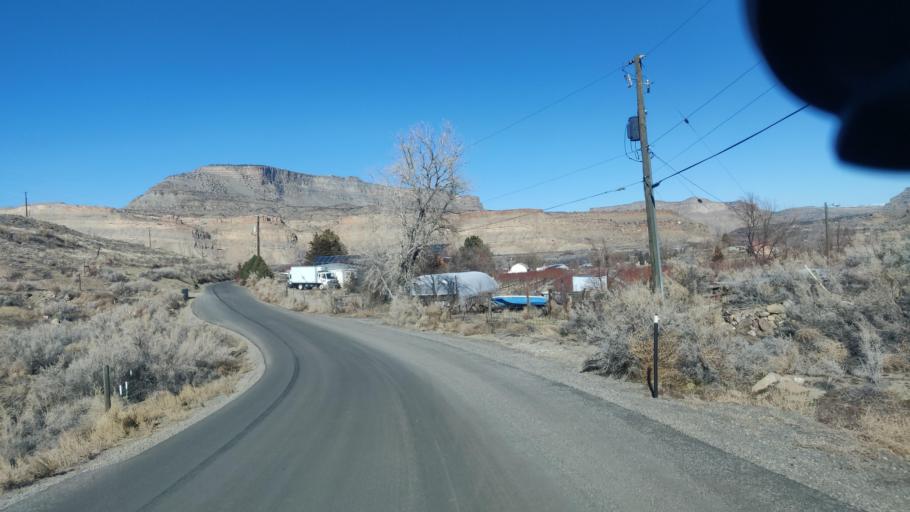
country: US
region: Colorado
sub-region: Mesa County
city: Palisade
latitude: 39.0985
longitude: -108.3296
